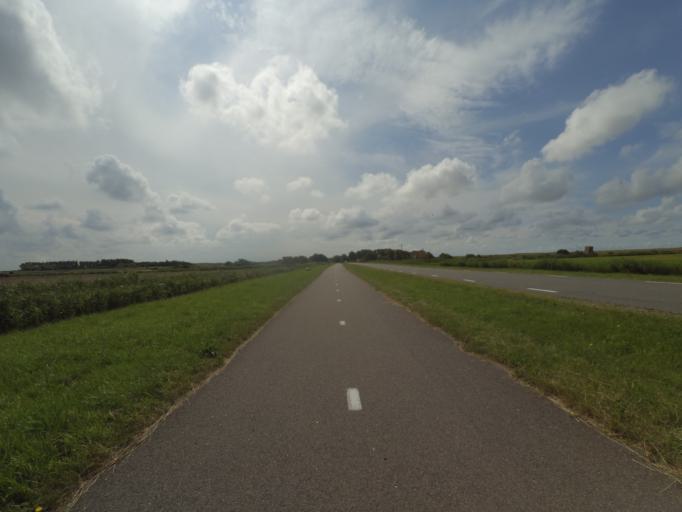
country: NL
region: North Holland
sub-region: Gemeente Texel
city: Den Burg
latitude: 53.0150
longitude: 4.7651
